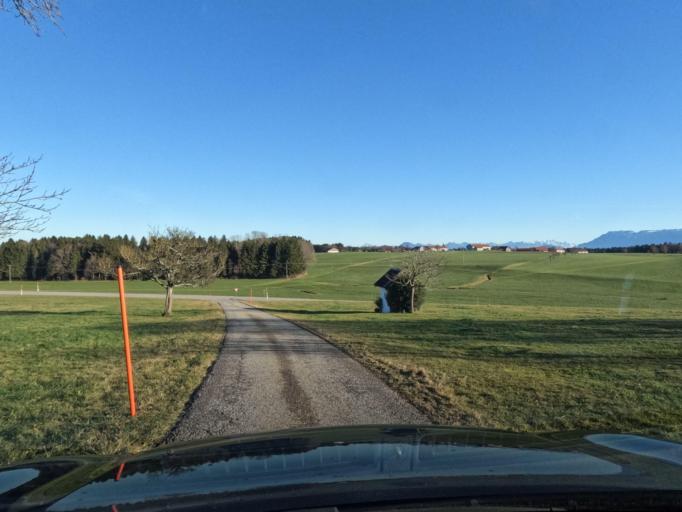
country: DE
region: Bavaria
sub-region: Upper Bavaria
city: Sankt Leonhard am Wonneberg
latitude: 47.8945
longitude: 12.7126
